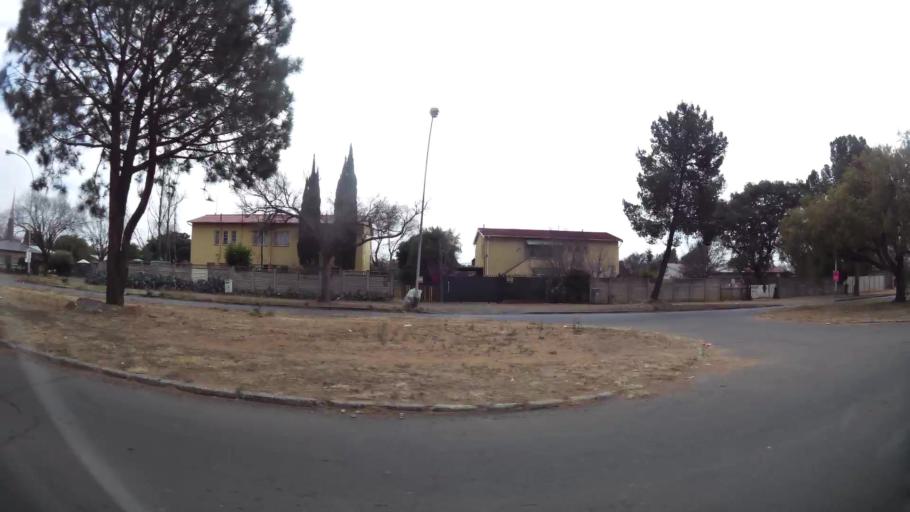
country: ZA
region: Orange Free State
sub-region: Mangaung Metropolitan Municipality
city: Bloemfontein
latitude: -29.1312
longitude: 26.1861
